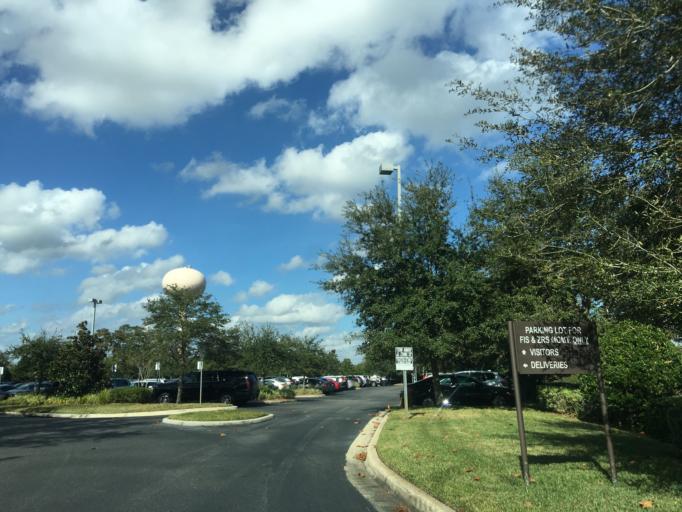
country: US
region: Florida
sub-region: Orange County
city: Eatonville
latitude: 28.6389
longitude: -81.4031
